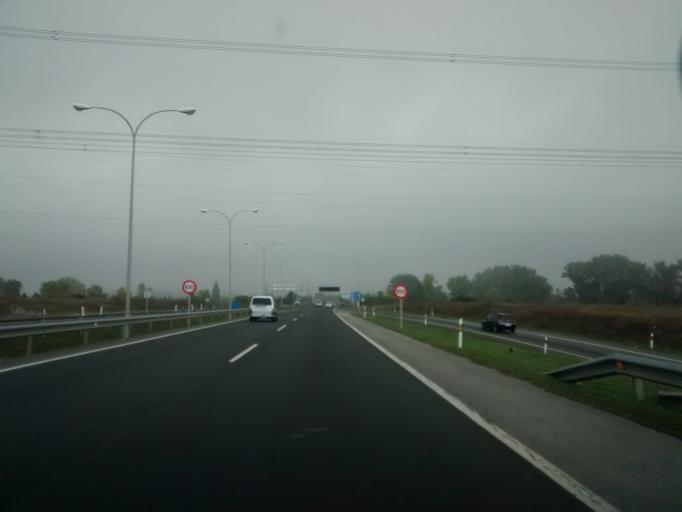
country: ES
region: Basque Country
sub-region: Provincia de Alava
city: Gasteiz / Vitoria
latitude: 42.8737
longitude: -2.6915
